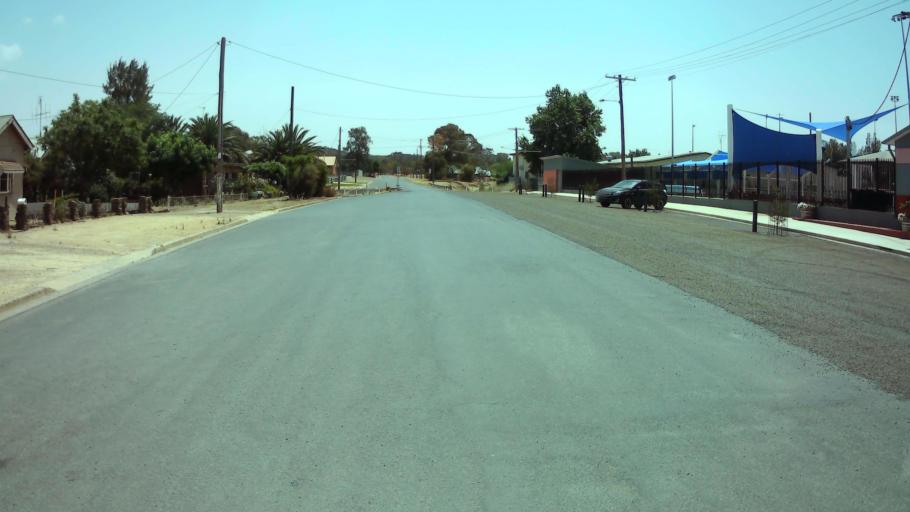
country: AU
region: New South Wales
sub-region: Weddin
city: Grenfell
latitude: -33.8922
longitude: 148.1604
